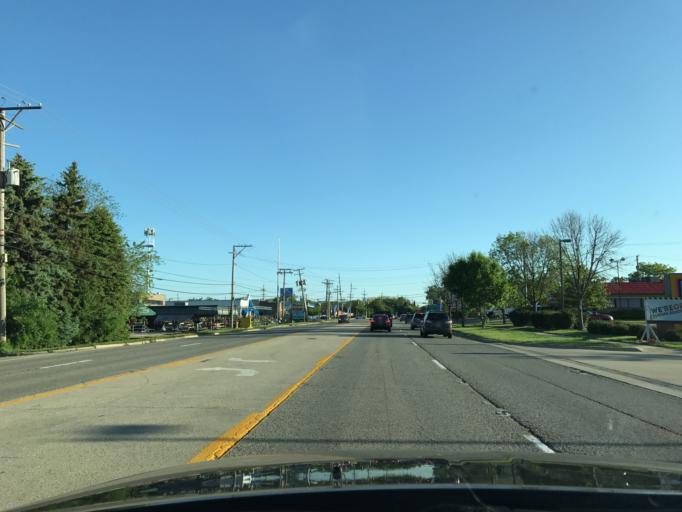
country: US
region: Illinois
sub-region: DuPage County
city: Lisle
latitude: 41.7846
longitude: -88.0737
